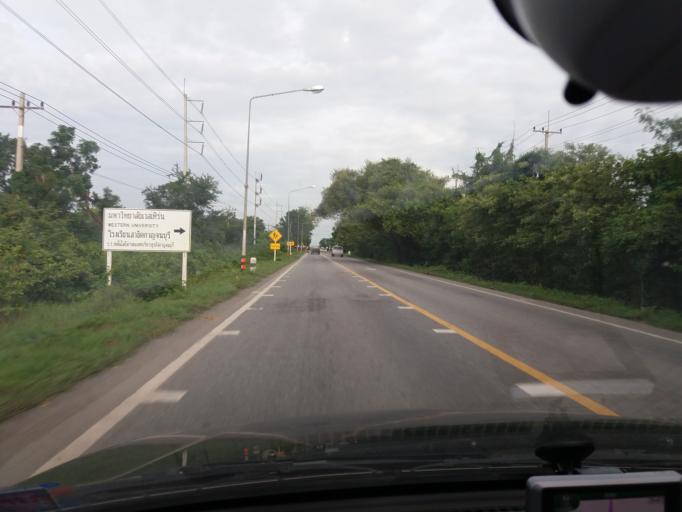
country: TH
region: Suphan Buri
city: U Thong
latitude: 14.3359
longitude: 99.8045
